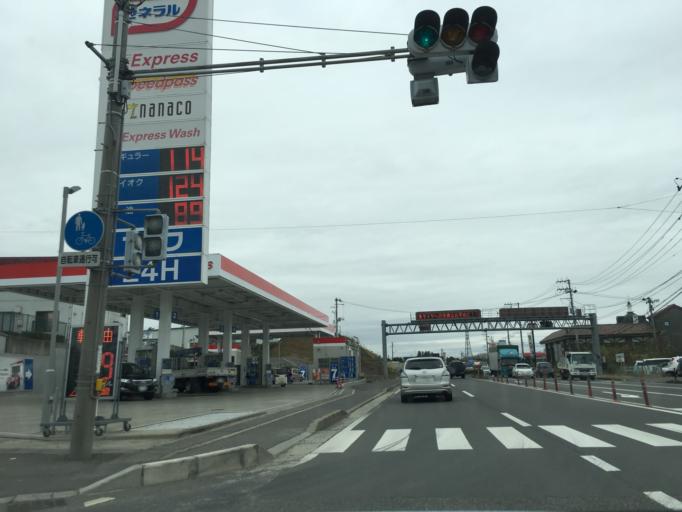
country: JP
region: Fukushima
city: Sukagawa
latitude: 37.3326
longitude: 140.3614
